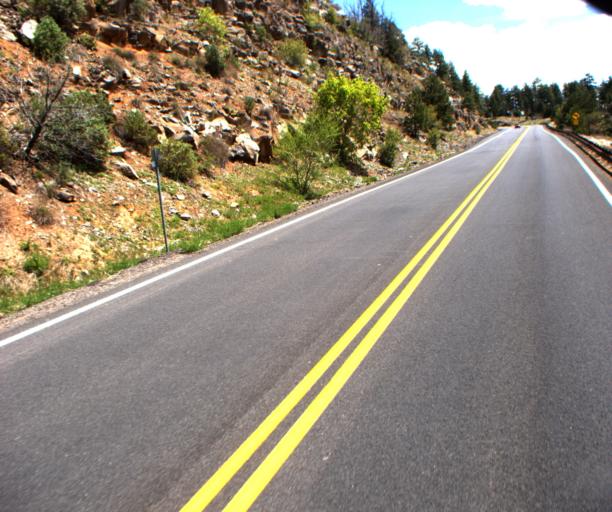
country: US
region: Arizona
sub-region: Coconino County
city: Kachina Village
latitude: 35.0295
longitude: -111.7381
